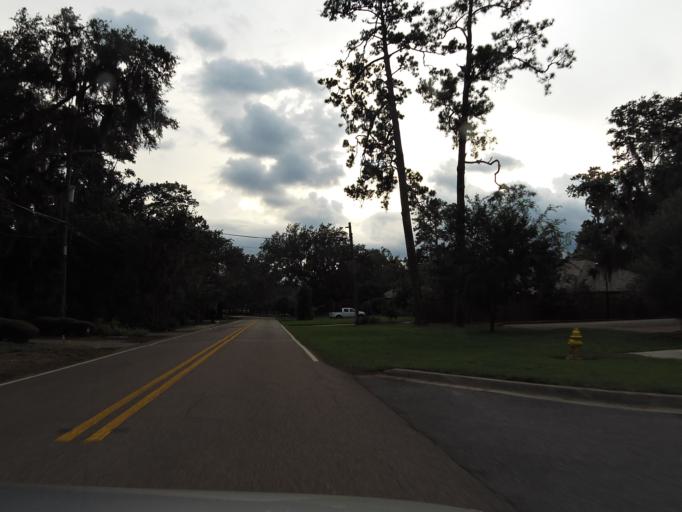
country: US
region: Florida
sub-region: Duval County
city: Jacksonville
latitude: 30.2725
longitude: -81.7022
